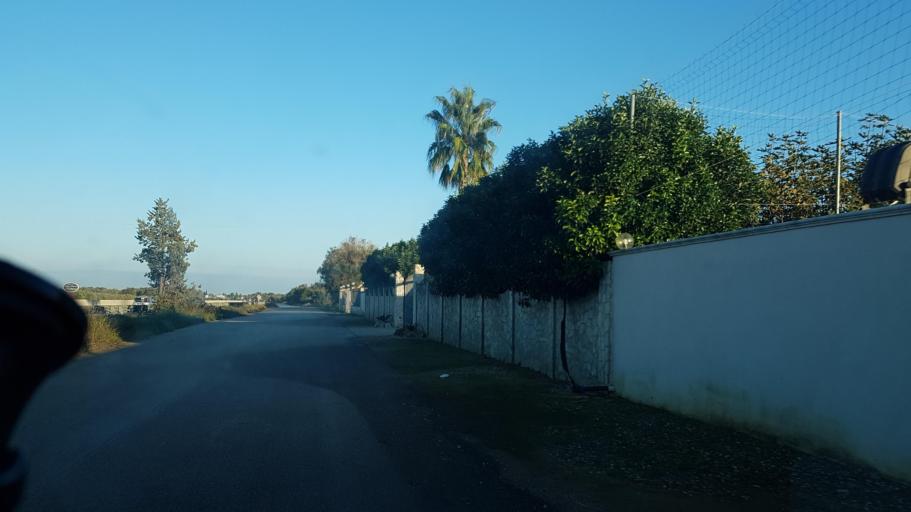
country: IT
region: Apulia
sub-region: Provincia di Brindisi
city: Mesagne
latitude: 40.5647
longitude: 17.7659
